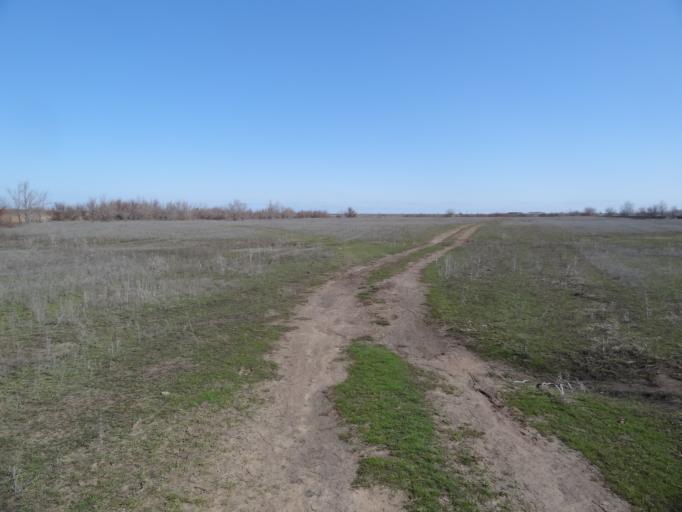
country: RU
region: Saratov
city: Shumeyka
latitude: 51.4156
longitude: 46.3029
